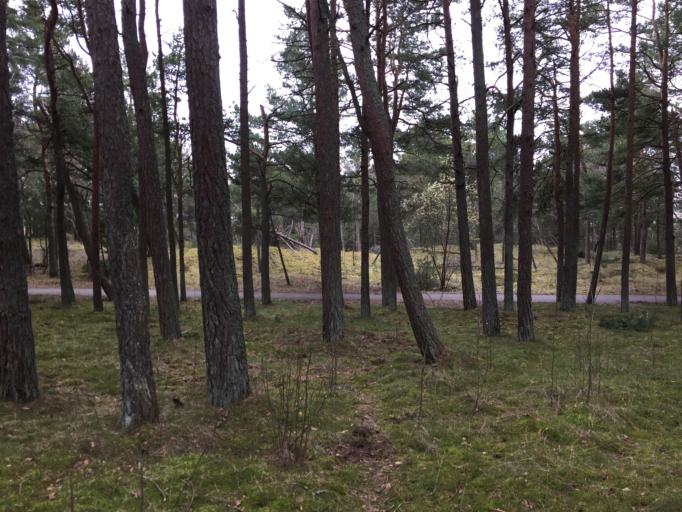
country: LT
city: Nida
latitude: 55.3046
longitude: 20.9965
